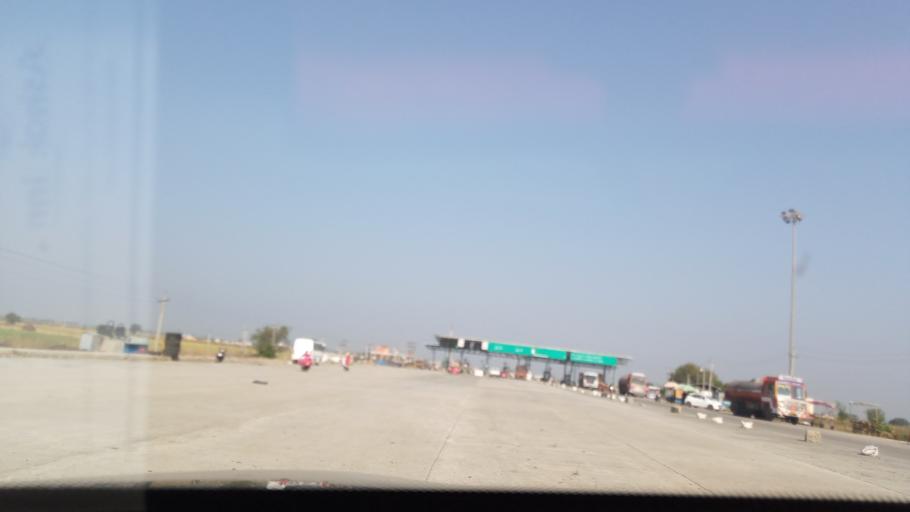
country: IN
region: Karnataka
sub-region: Haveri
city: Savanur
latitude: 14.9088
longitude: 75.2810
